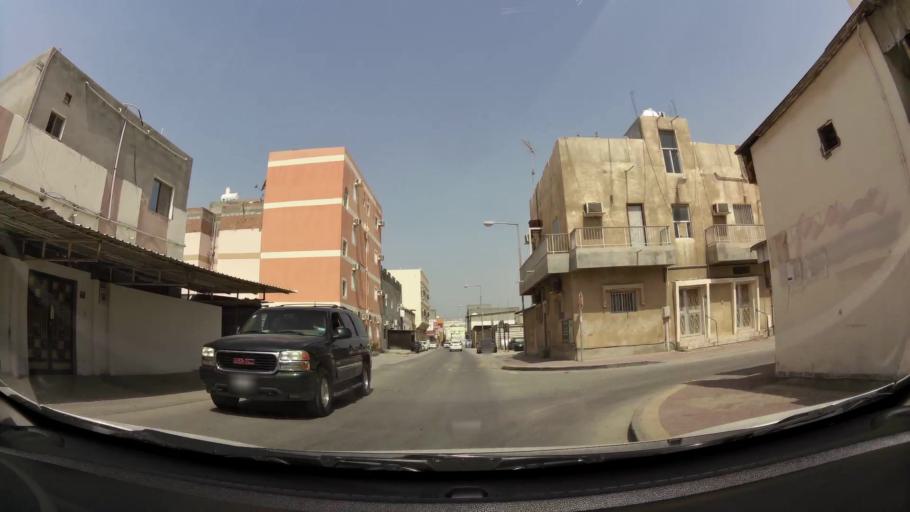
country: BH
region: Manama
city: Jidd Hafs
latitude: 26.2276
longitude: 50.4805
